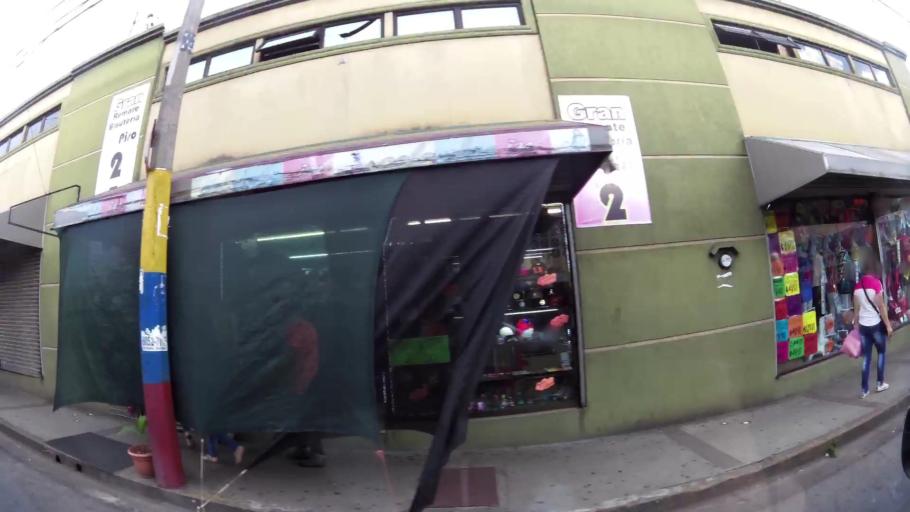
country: CR
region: Alajuela
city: Alajuela
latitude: 10.0171
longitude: -84.2172
